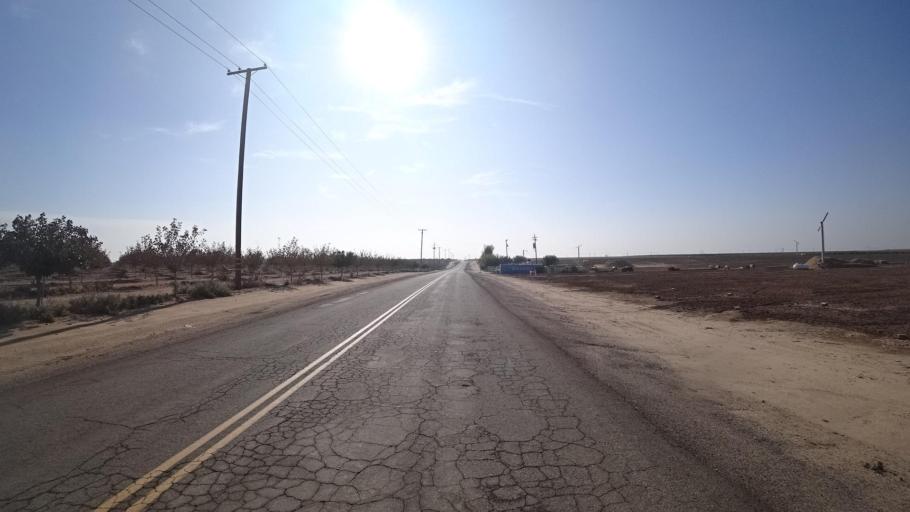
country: US
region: California
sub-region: Kern County
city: McFarland
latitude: 35.6363
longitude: -119.1689
